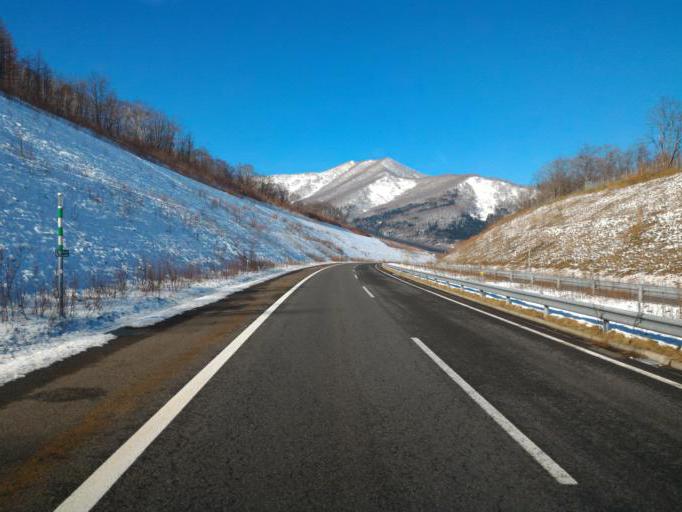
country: JP
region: Hokkaido
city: Otofuke
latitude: 43.0335
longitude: 142.7918
